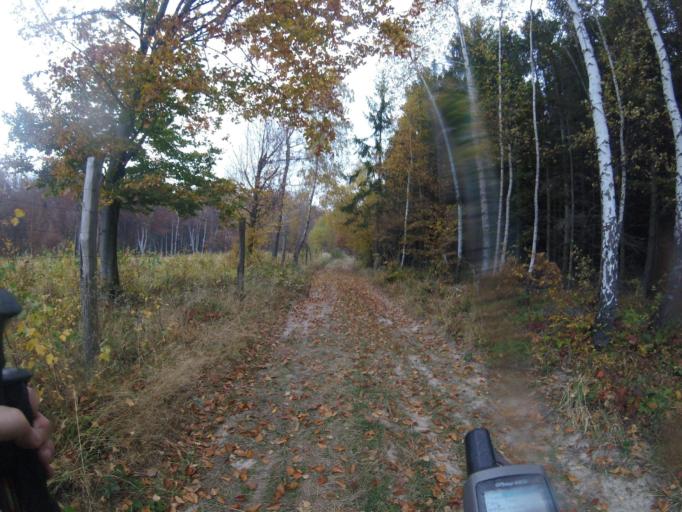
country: HU
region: Borsod-Abauj-Zemplen
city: Gonc
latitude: 48.4431
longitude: 21.3274
